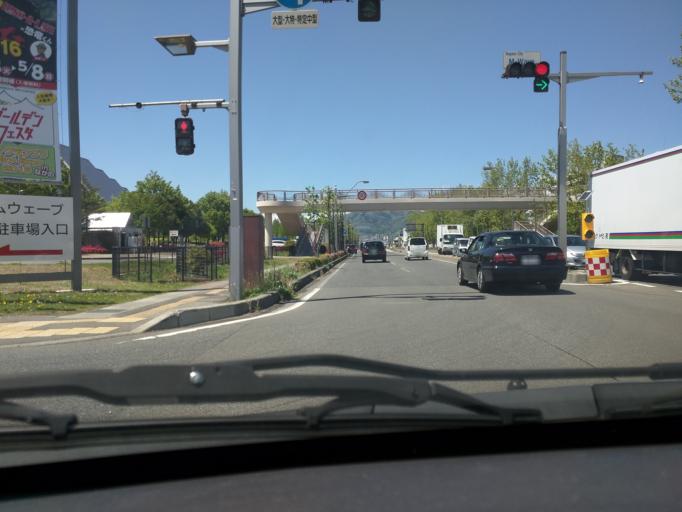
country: JP
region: Nagano
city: Nagano-shi
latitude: 36.6420
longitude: 138.2433
